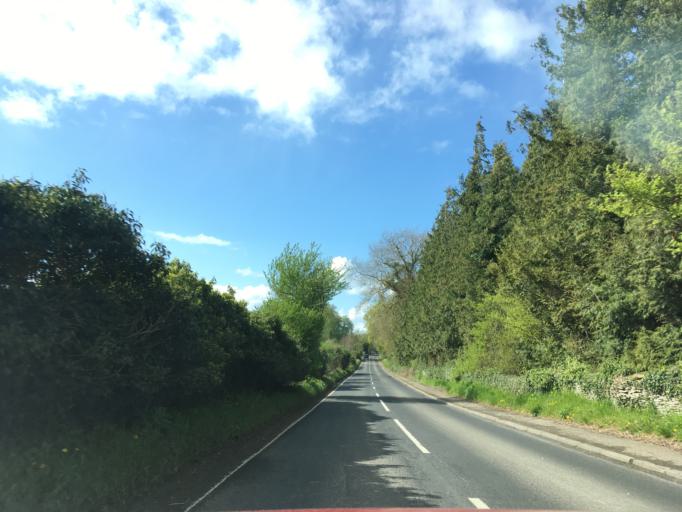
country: GB
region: England
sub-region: Gloucestershire
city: Tetbury
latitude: 51.6507
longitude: -2.1713
